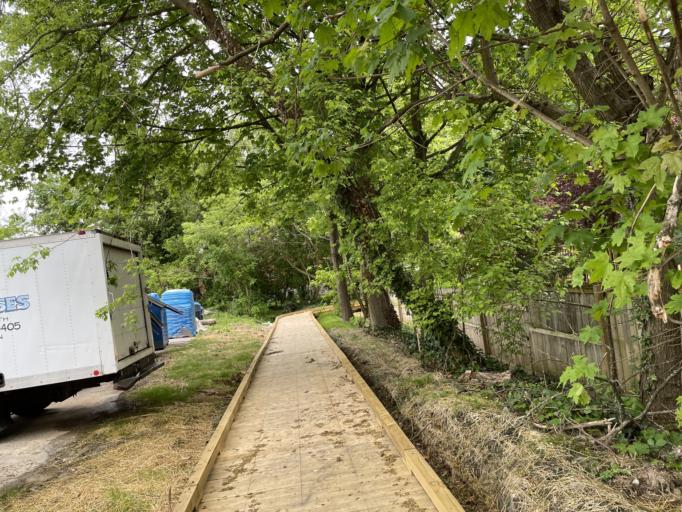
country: US
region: Maryland
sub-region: Baltimore County
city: Towson
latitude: 39.3930
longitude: -76.5979
